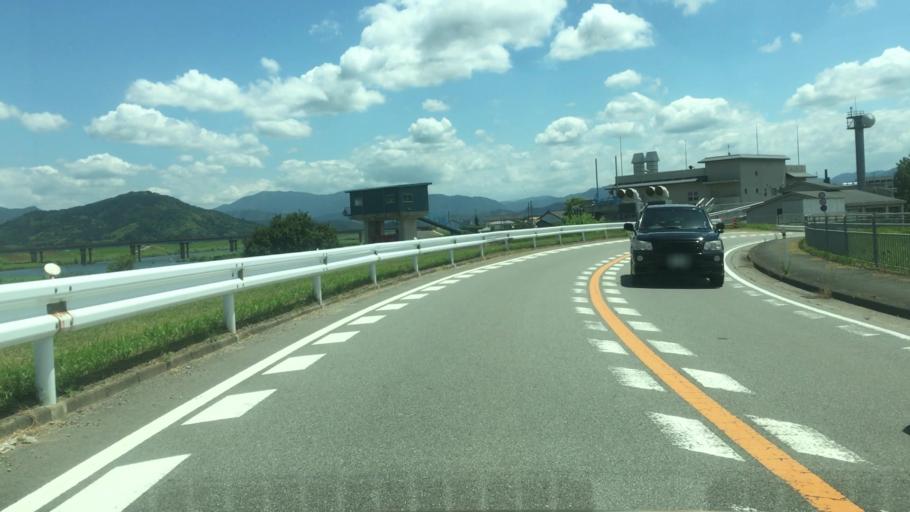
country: JP
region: Hyogo
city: Toyooka
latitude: 35.5479
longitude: 134.8262
